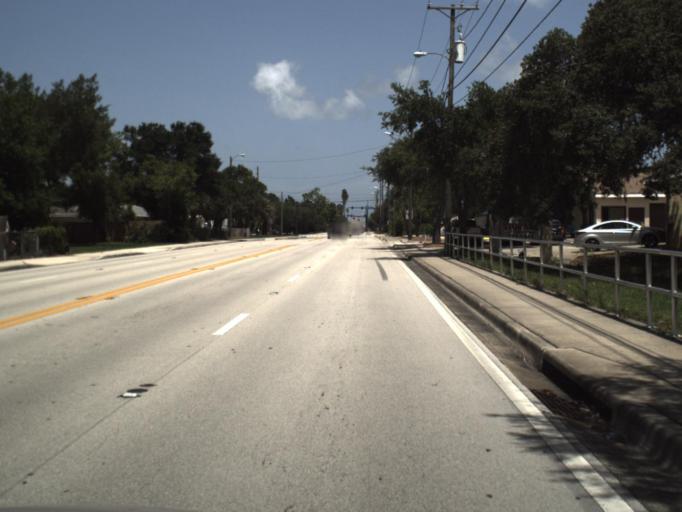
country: US
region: Florida
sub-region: Pinellas County
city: Clearwater
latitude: 27.9789
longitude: -82.7959
